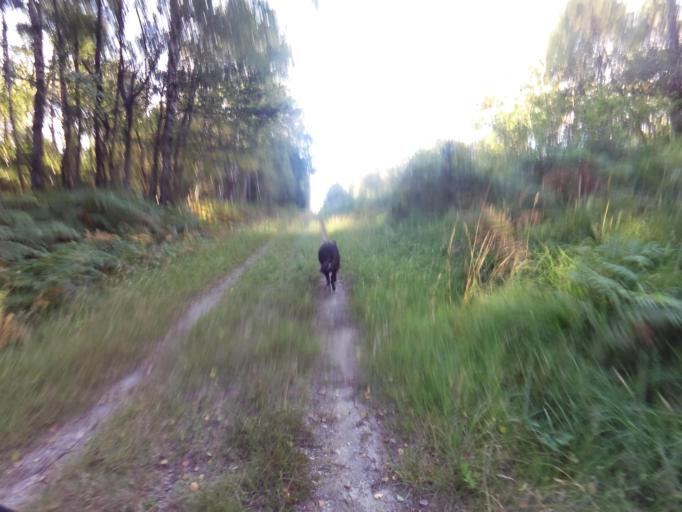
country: FR
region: Brittany
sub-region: Departement du Morbihan
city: Molac
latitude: 47.7478
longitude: -2.4303
